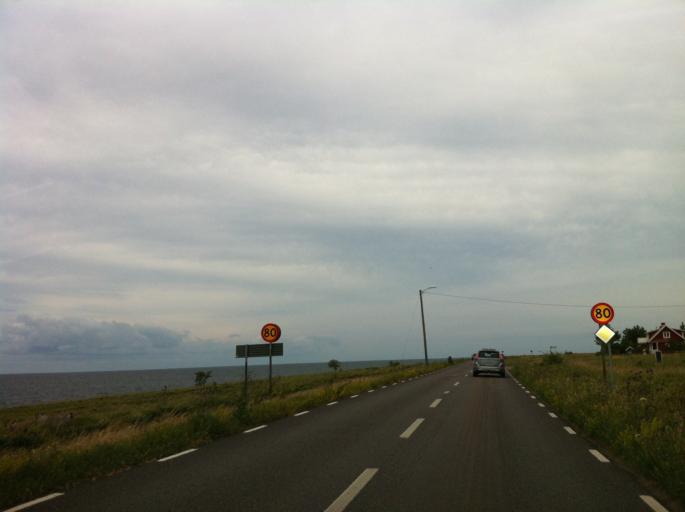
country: SE
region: Kalmar
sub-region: Oskarshamns Kommun
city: Oskarshamn
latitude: 57.3314
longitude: 17.0087
